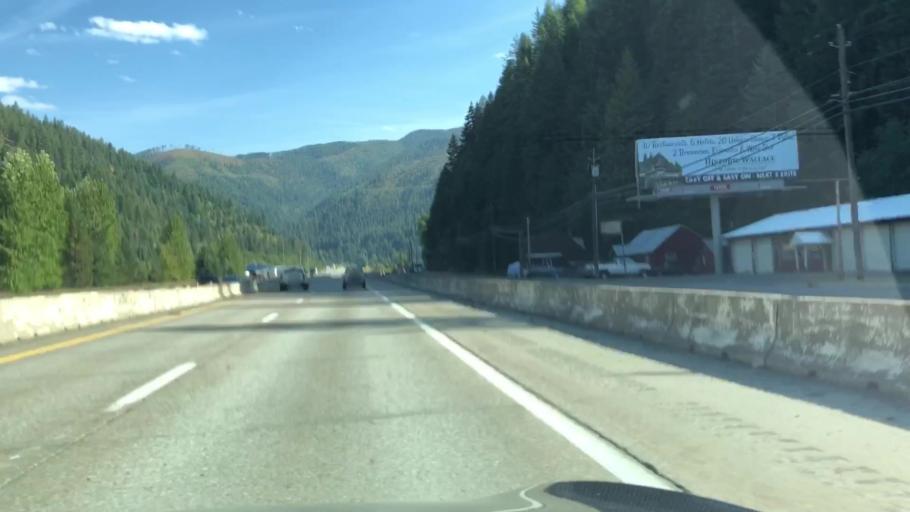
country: US
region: Idaho
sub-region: Shoshone County
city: Wallace
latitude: 47.4841
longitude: -115.9415
